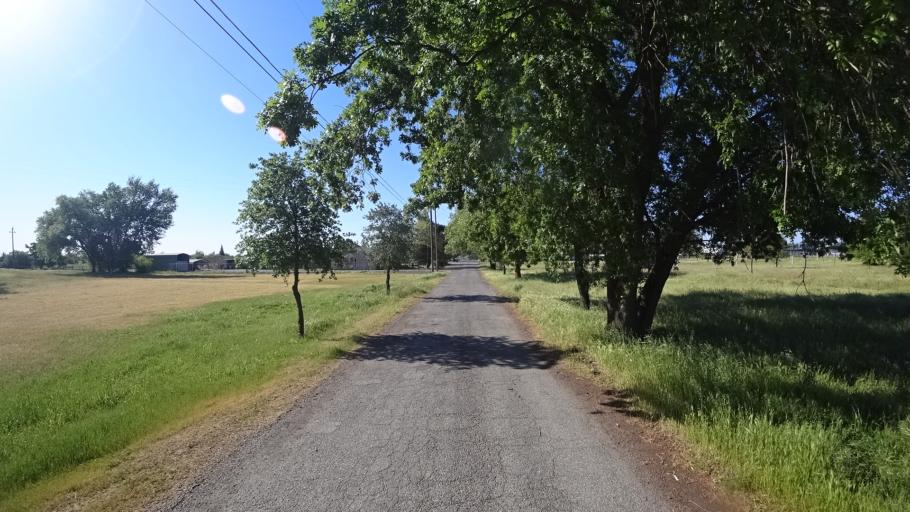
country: US
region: California
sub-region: Glenn County
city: Orland
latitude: 39.7558
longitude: -122.1888
